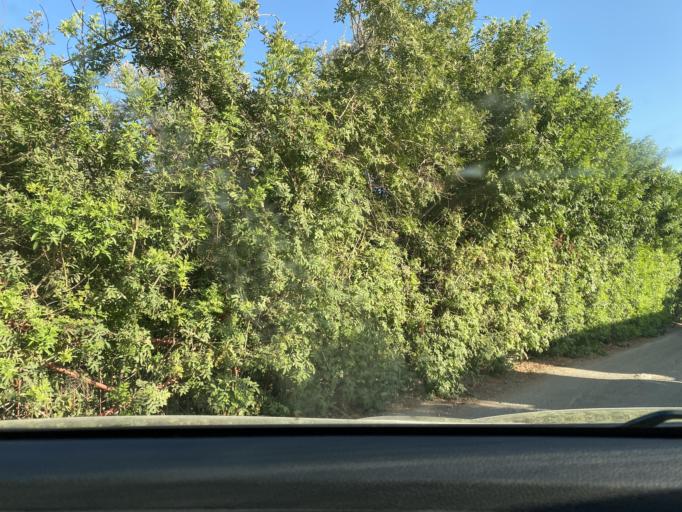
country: IL
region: Northern District
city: Shelomi
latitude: 33.0685
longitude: 35.1382
